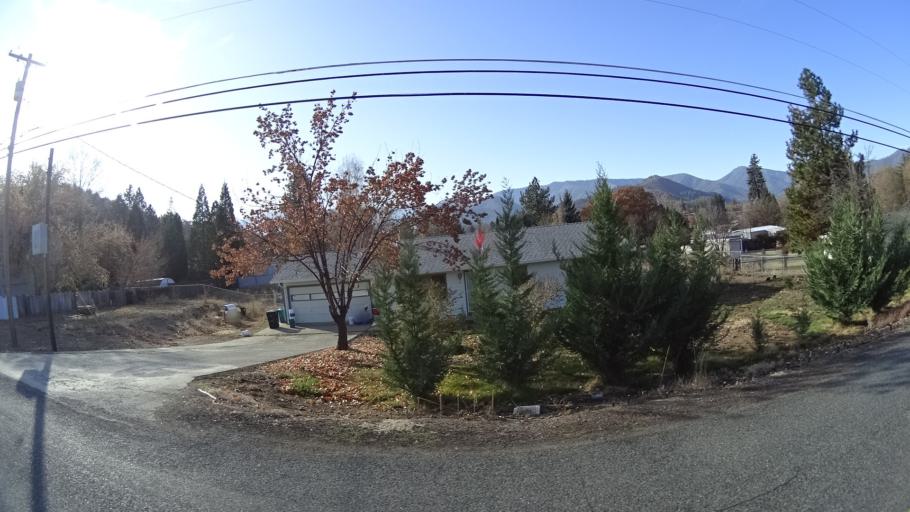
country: US
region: California
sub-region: Siskiyou County
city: Yreka
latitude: 41.6996
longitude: -122.6352
